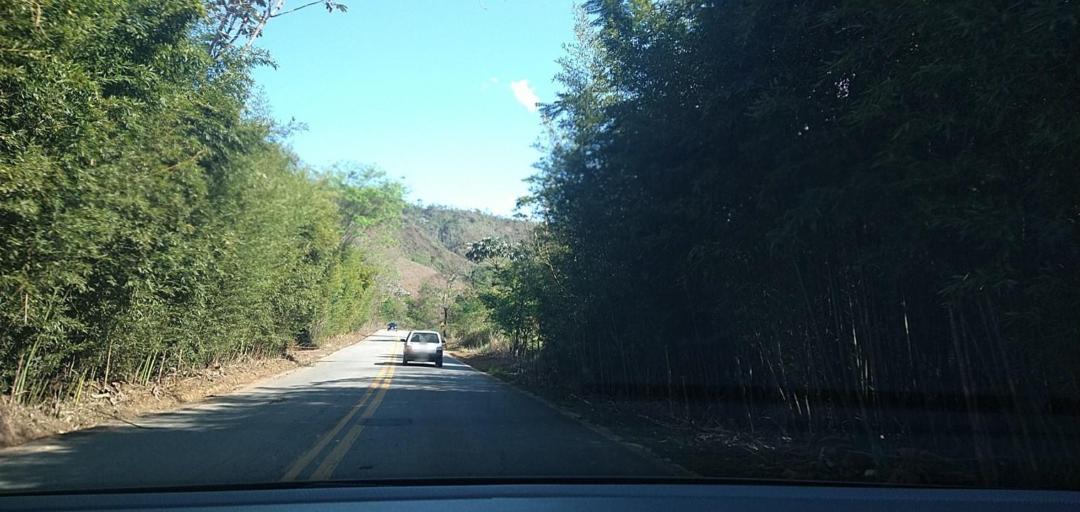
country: BR
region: Minas Gerais
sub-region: Alvinopolis
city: Alvinopolis
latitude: -20.0400
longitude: -43.0323
